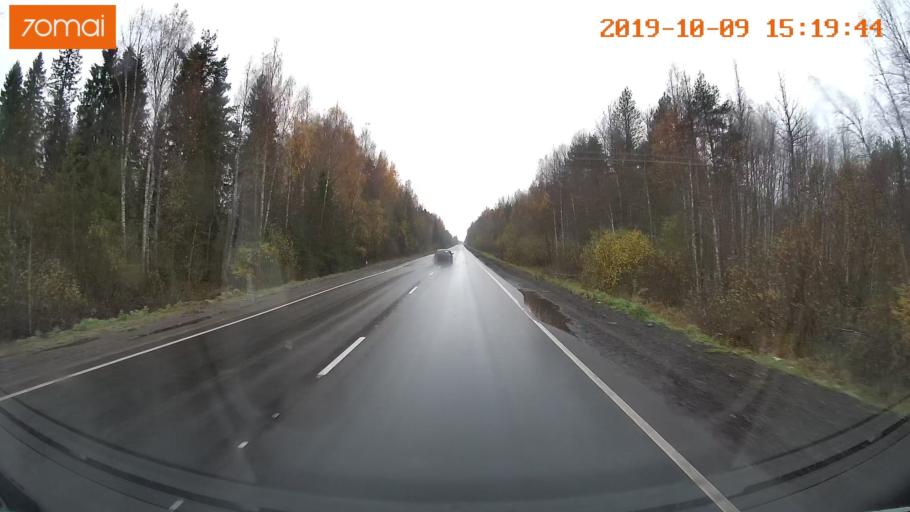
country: RU
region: Kostroma
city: Susanino
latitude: 58.0723
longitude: 41.5510
